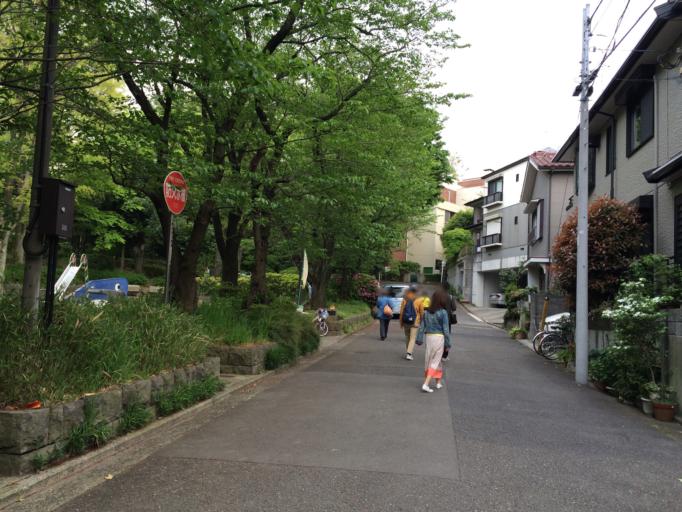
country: JP
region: Kanagawa
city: Yokohama
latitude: 35.5241
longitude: 139.6315
